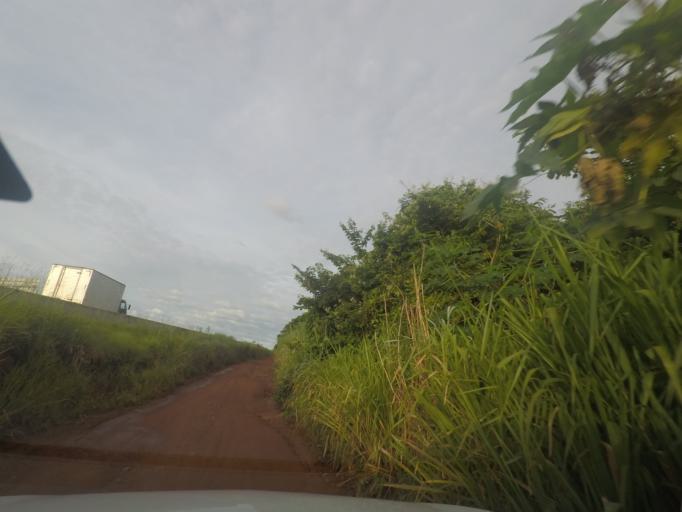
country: BR
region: Goias
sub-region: Trindade
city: Trindade
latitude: -16.7374
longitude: -49.4070
